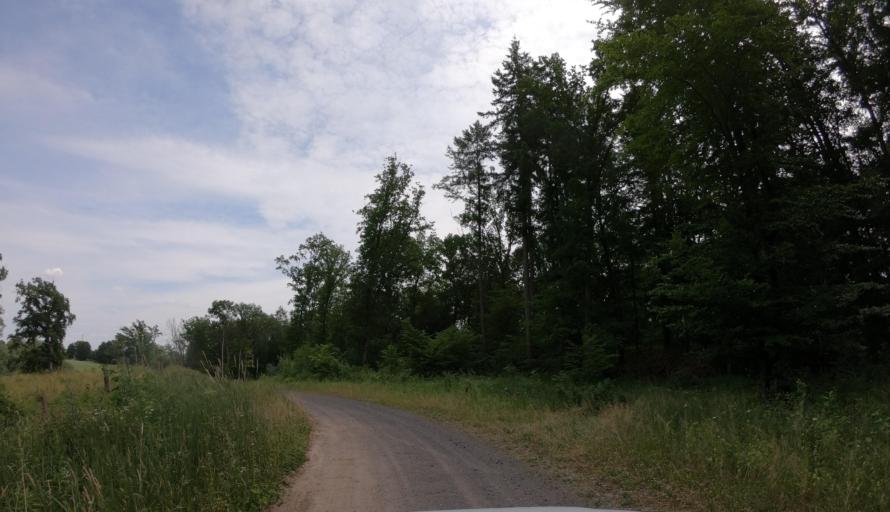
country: PL
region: West Pomeranian Voivodeship
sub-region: Powiat pyrzycki
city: Kozielice
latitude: 53.0288
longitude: 14.7496
